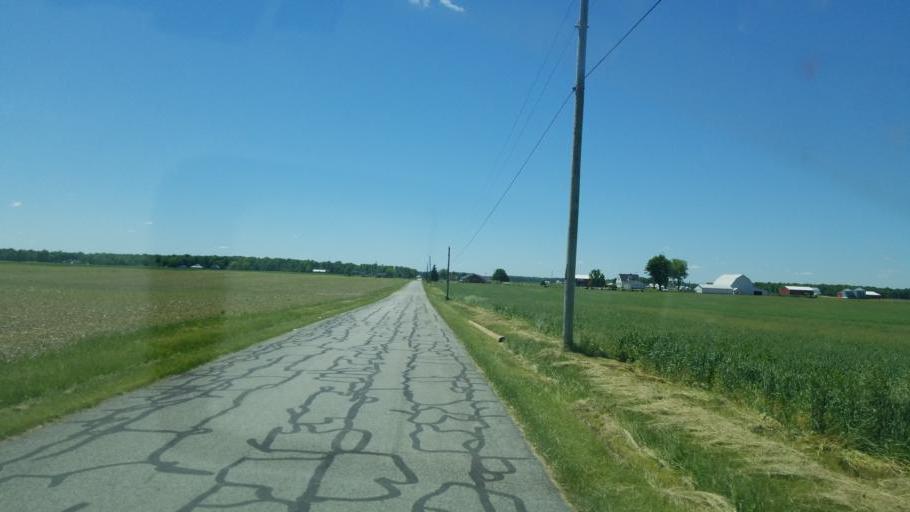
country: US
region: Ohio
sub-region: Shelby County
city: Fort Loramie
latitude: 40.3679
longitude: -84.3166
